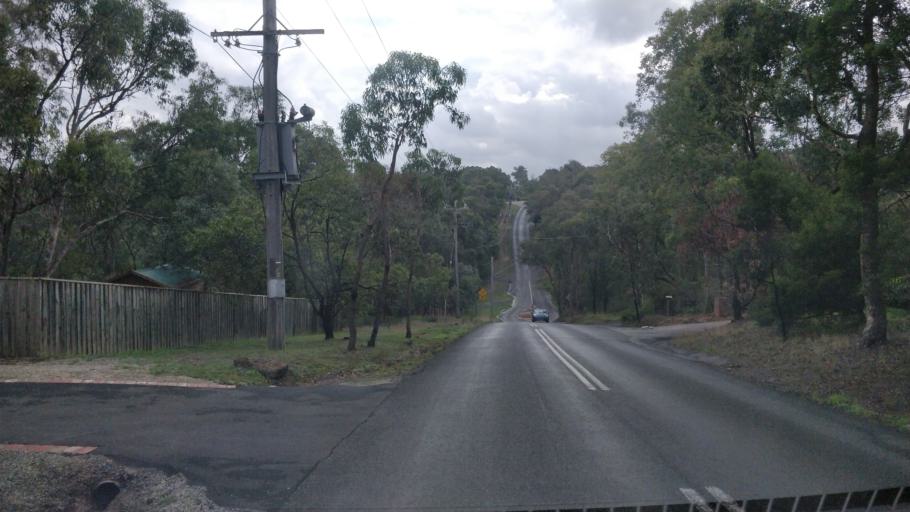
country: AU
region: Victoria
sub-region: Nillumbik
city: Research
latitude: -37.7132
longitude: 145.1745
